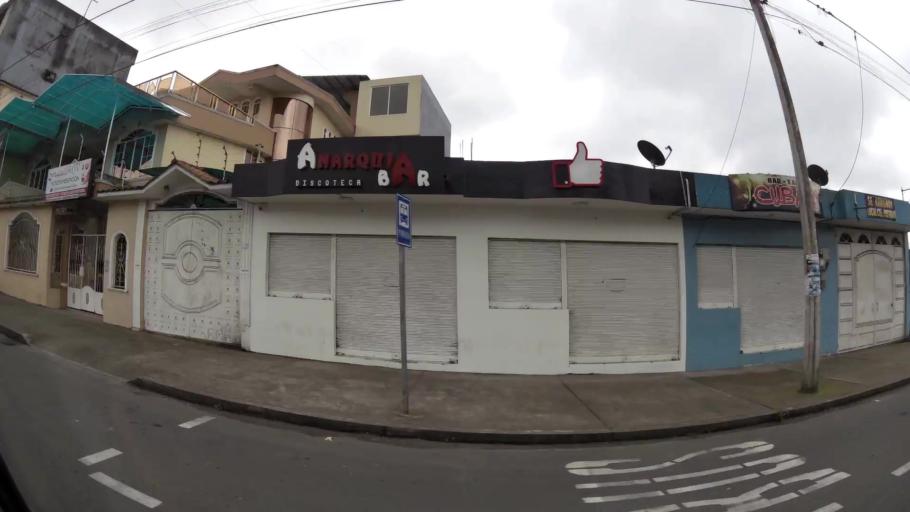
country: EC
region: Santo Domingo de los Tsachilas
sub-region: Canton Santo Domingo de los Colorados
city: Santo Domingo de los Colorados
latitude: -0.2580
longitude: -79.1502
